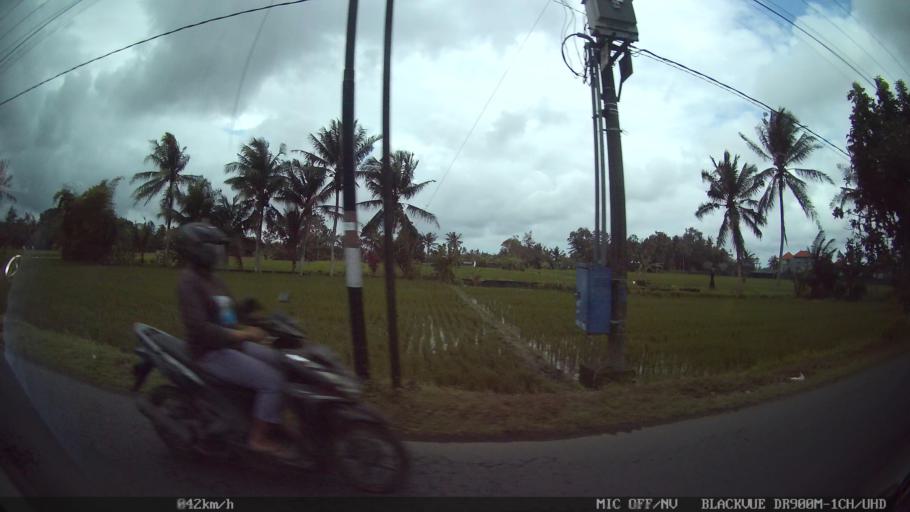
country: ID
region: Bali
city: Banjar Pekenjelodan
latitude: -8.5582
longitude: 115.1894
